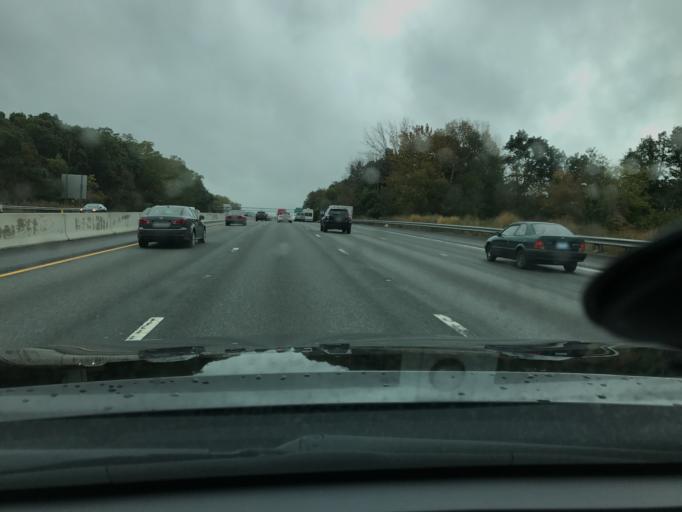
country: US
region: Massachusetts
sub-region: Middlesex County
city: Waltham
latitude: 42.4082
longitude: -71.2587
